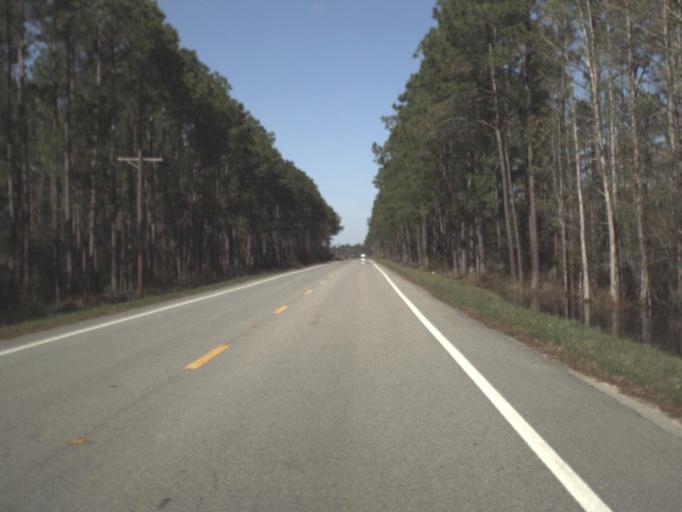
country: US
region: Florida
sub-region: Gulf County
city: Wewahitchka
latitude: 29.9634
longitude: -85.1741
